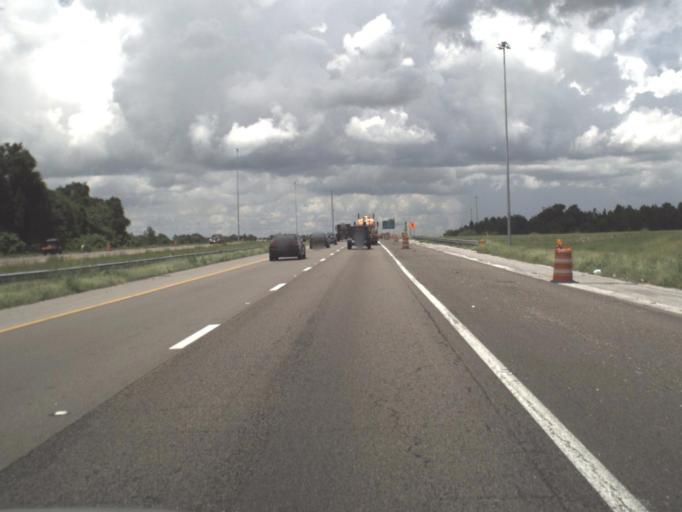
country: US
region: Florida
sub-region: Hillsborough County
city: Temple Terrace
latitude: 28.0505
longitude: -82.3528
